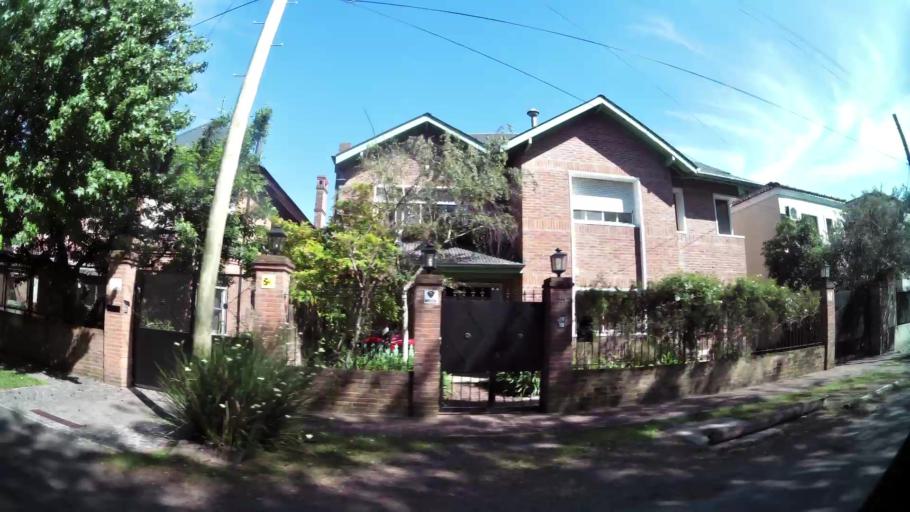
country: AR
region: Buenos Aires
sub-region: Partido de Tigre
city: Tigre
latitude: -34.4796
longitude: -58.5748
